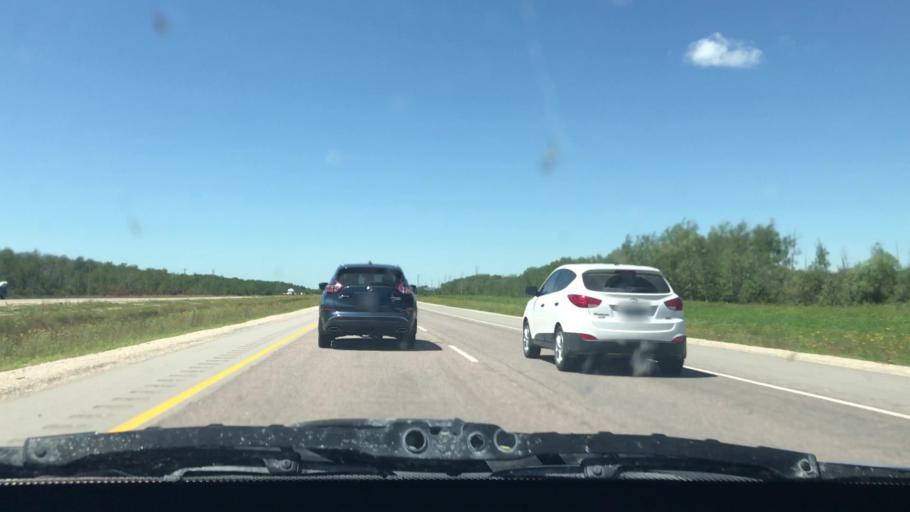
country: CA
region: Manitoba
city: La Broquerie
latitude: 49.6754
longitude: -96.5814
